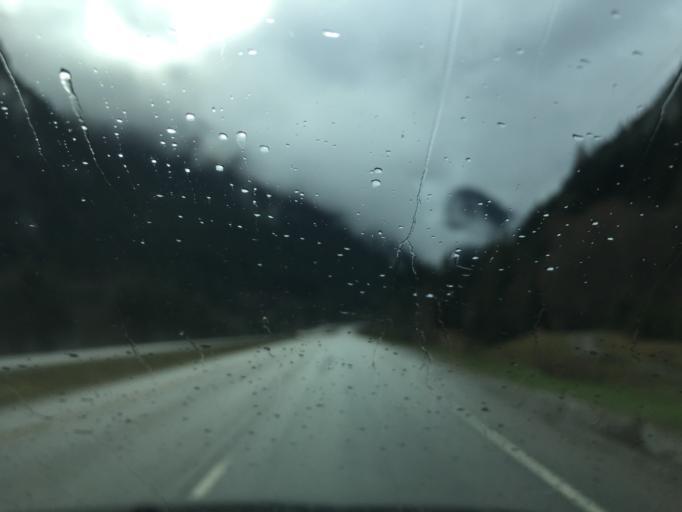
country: CA
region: British Columbia
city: Hope
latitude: 49.4463
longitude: -121.2728
